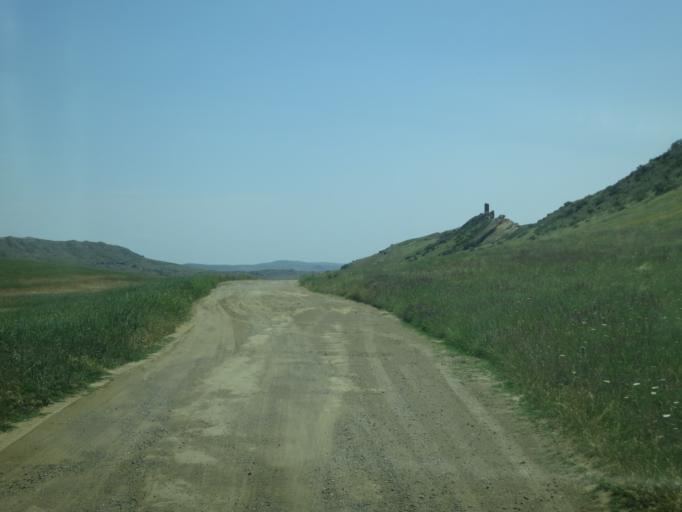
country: AZ
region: Agstafa
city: Saloglu
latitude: 41.4615
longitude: 45.3428
